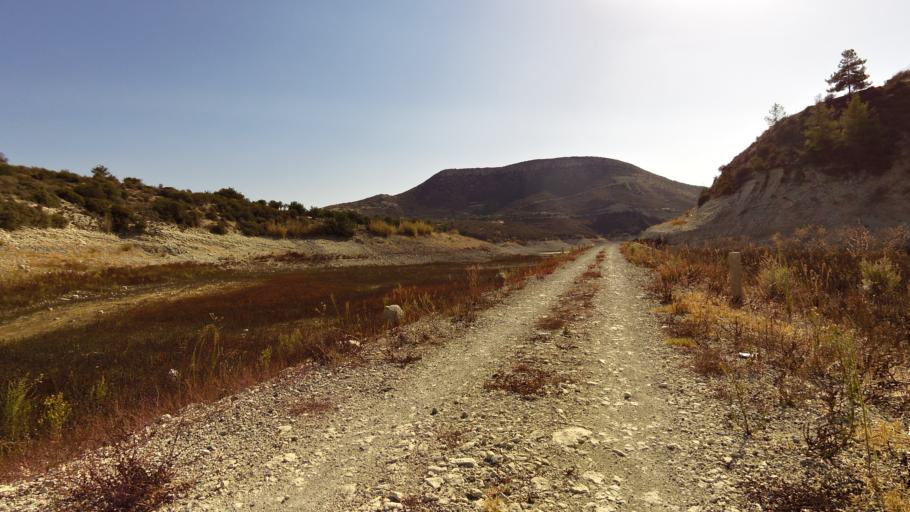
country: CY
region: Limassol
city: Mouttagiaka
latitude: 34.7549
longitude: 33.0853
